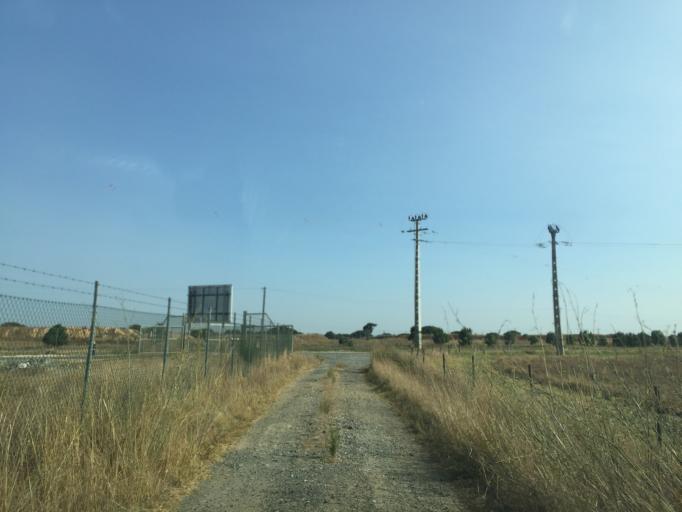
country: PT
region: Beja
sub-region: Aljustrel
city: Aljustrel
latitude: 38.0221
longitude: -8.3579
